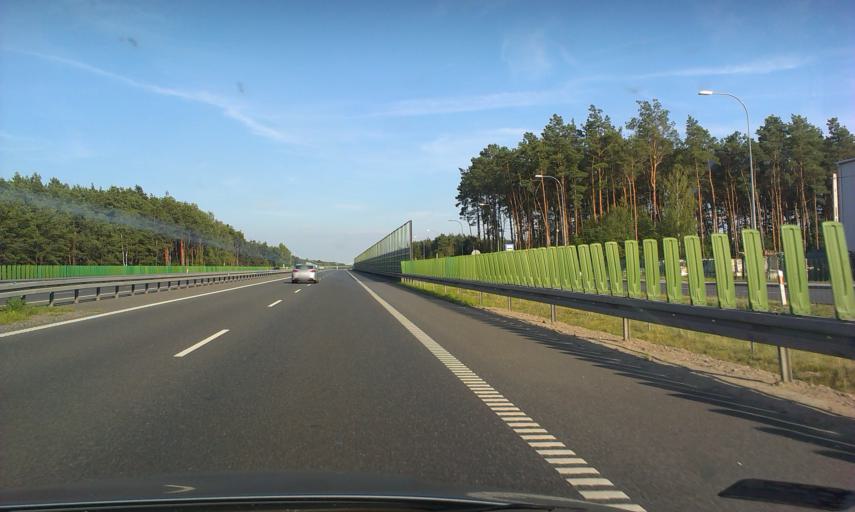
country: PL
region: Kujawsko-Pomorskie
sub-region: Powiat bydgoski
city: Biale Blota
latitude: 53.0706
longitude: 17.9257
